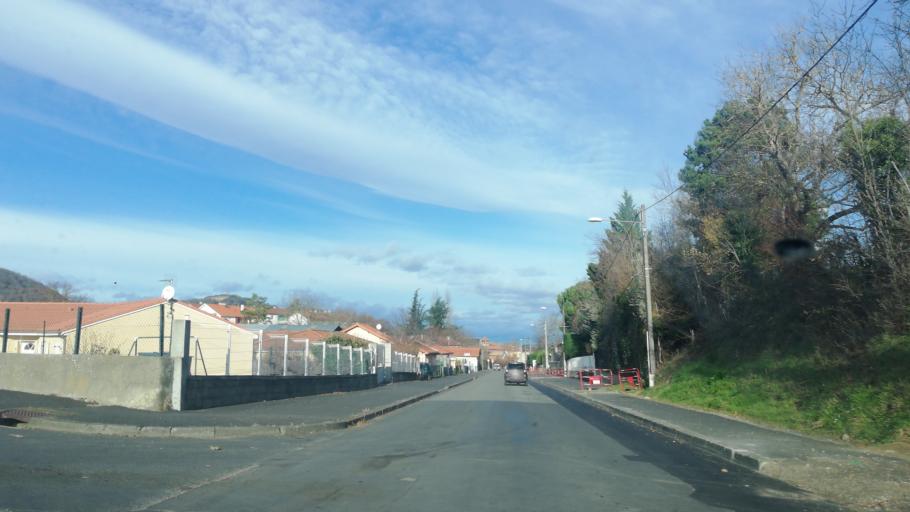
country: FR
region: Auvergne
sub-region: Departement du Puy-de-Dome
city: Billom
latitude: 45.7174
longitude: 3.3431
